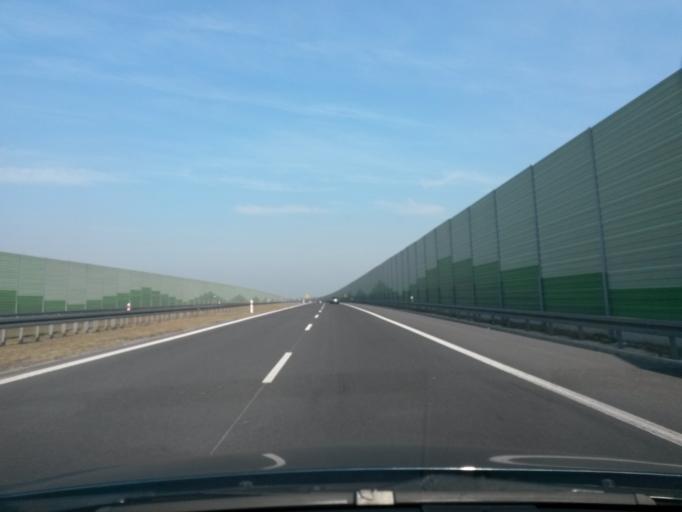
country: PL
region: Lodz Voivodeship
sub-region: Powiat leczycki
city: Piatek
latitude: 52.1100
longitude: 19.5084
